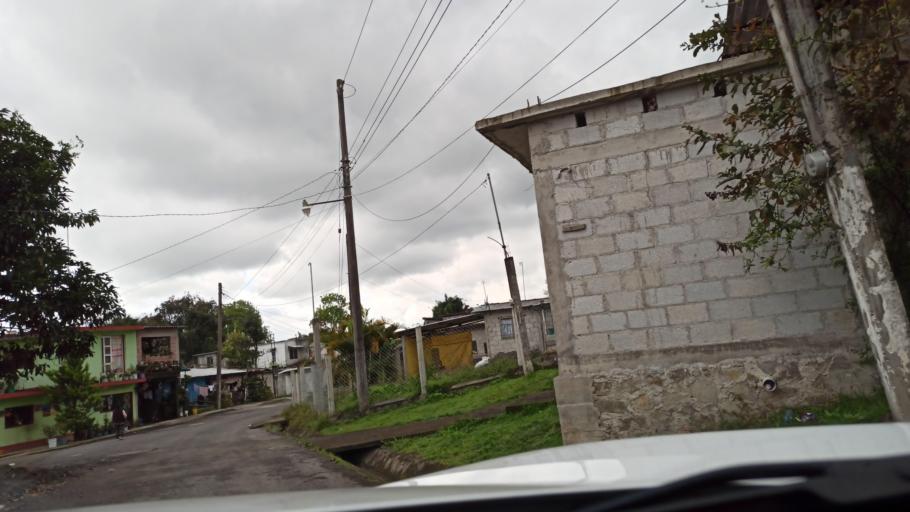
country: MX
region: Veracruz
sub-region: Chocaman
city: San Jose Neria
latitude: 19.0067
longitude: -97.0107
